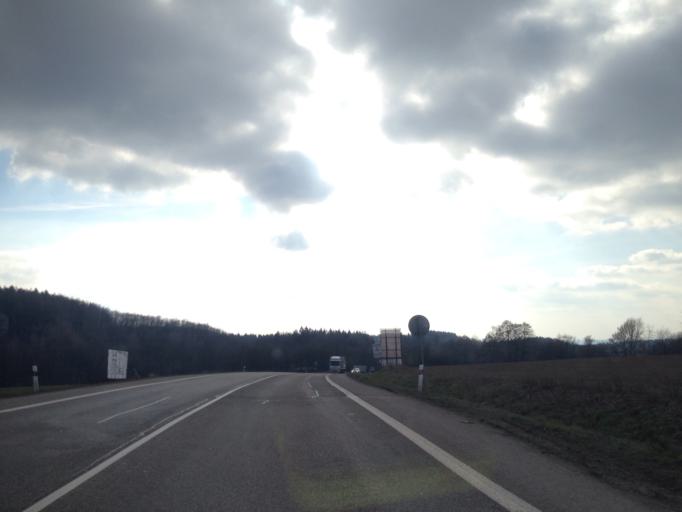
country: CZ
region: Kralovehradecky
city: Nova Paka
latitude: 50.4689
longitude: 15.4983
